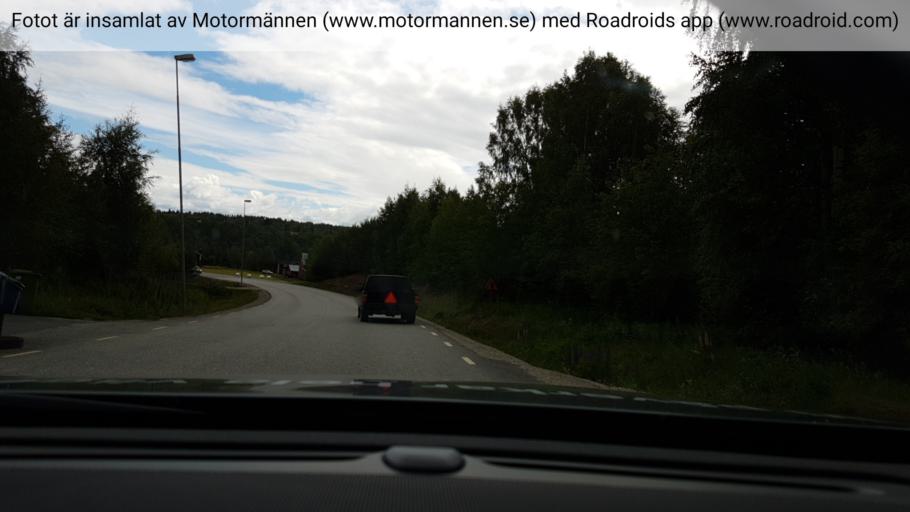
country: SE
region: Vaesterbotten
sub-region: Vindelns Kommun
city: Vindeln
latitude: 64.2012
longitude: 19.6893
